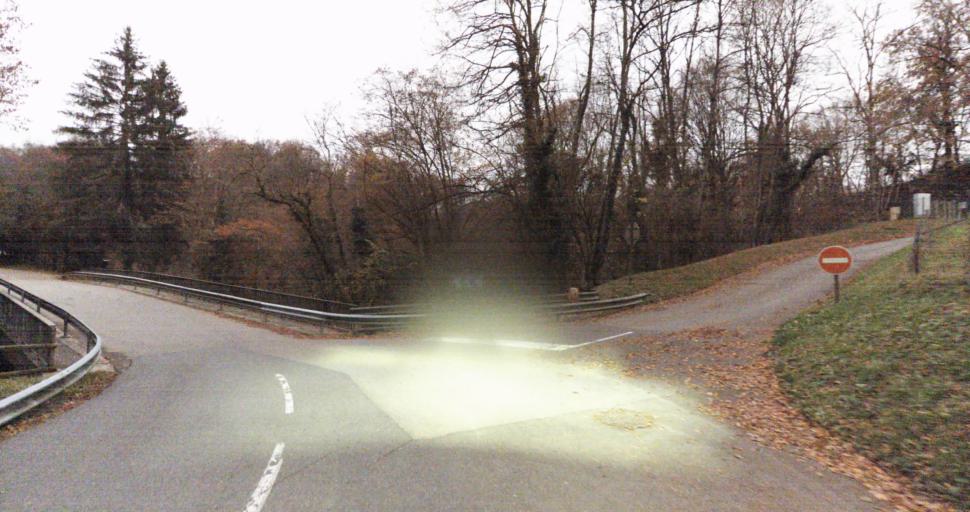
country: FR
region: Rhone-Alpes
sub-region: Departement de la Haute-Savoie
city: Alby-sur-Cheran
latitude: 45.8287
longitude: 6.0218
